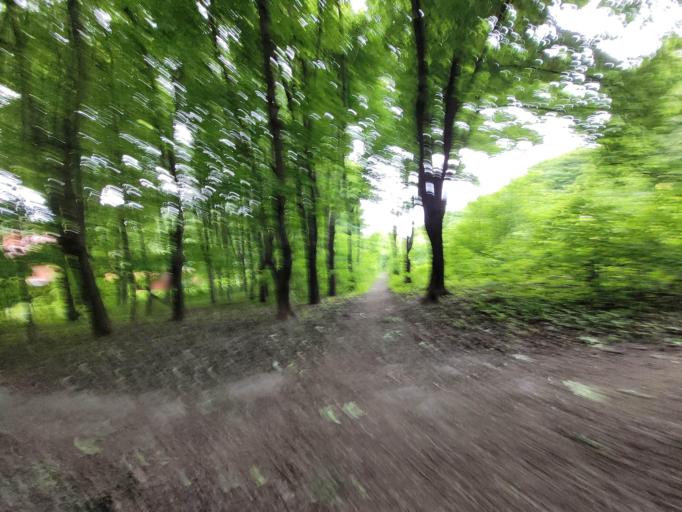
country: RU
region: Moskovskaya
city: Lesnyye Polyany
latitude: 55.9477
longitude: 37.8601
